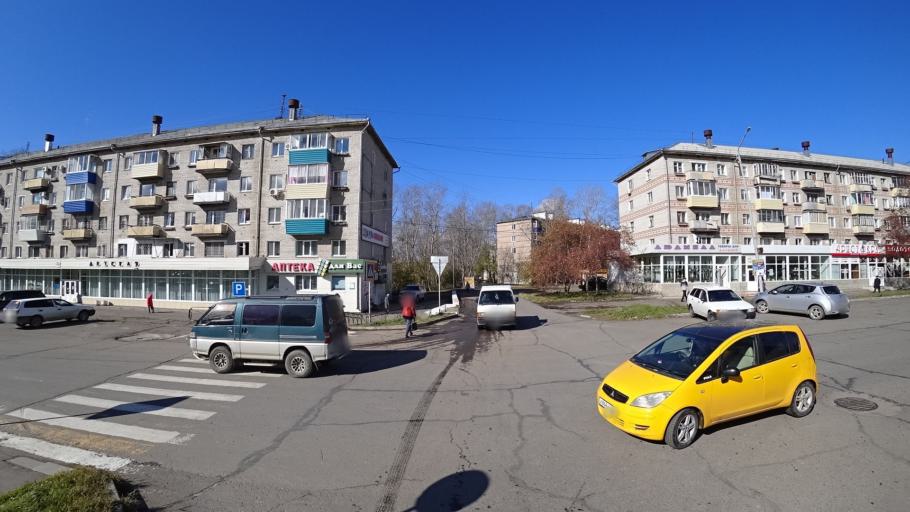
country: RU
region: Khabarovsk Krai
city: Amursk
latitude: 50.2256
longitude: 136.9082
